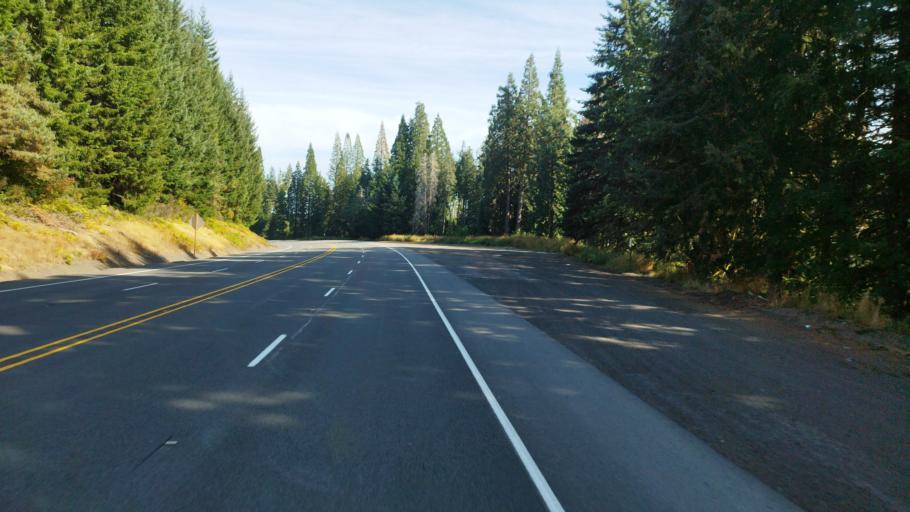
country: US
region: Oregon
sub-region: Columbia County
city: Vernonia
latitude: 45.7738
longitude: -123.3707
